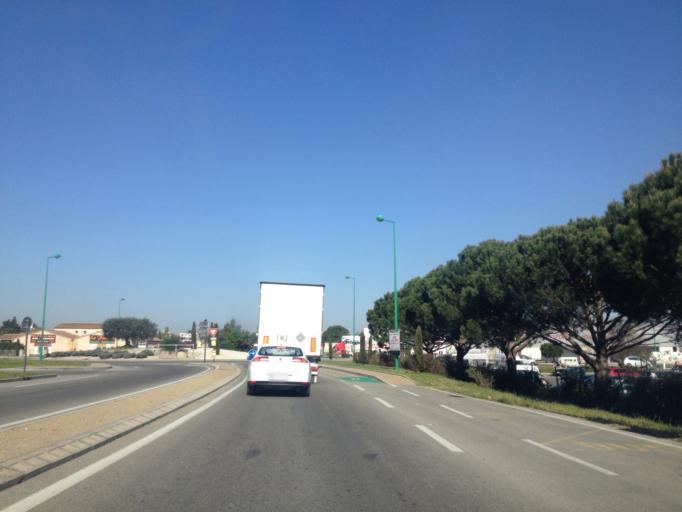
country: FR
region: Provence-Alpes-Cote d'Azur
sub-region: Departement du Vaucluse
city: Sarrians
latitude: 44.0806
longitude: 4.9828
